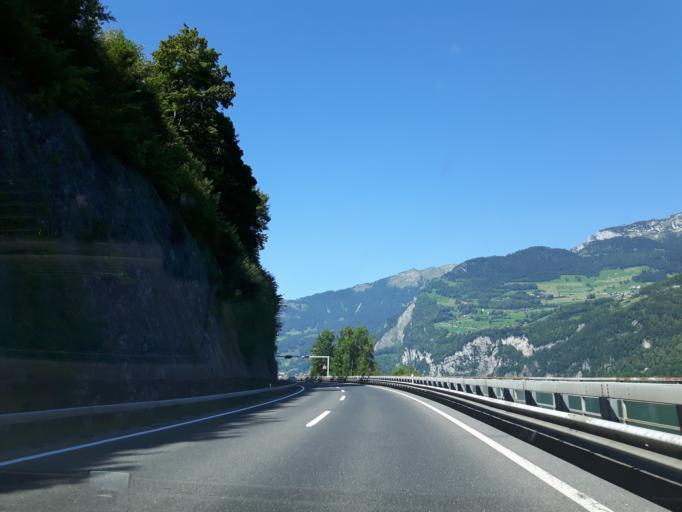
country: CH
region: Saint Gallen
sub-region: Wahlkreis See-Gaster
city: Amden
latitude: 47.1215
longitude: 9.1573
